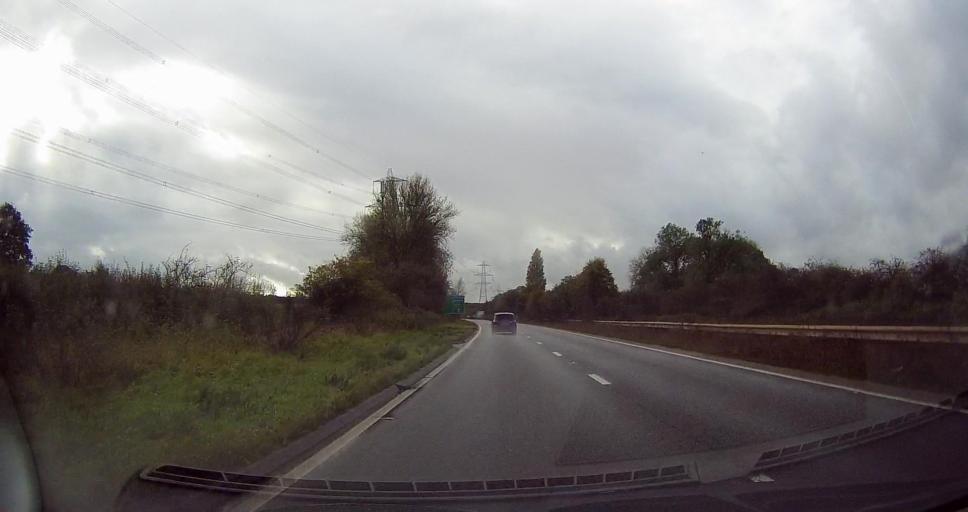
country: GB
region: England
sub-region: Staffordshire
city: Lichfield
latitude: 52.6690
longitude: -1.8101
